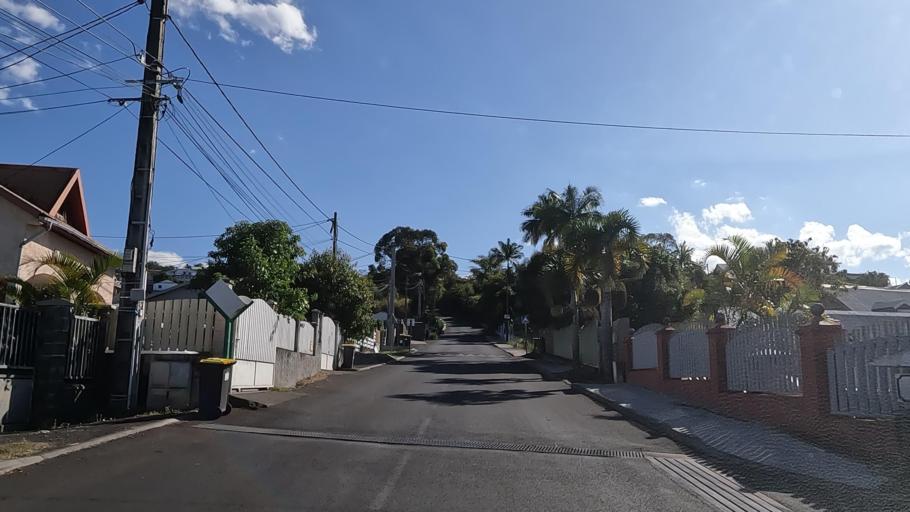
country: RE
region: Reunion
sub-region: Reunion
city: Le Tampon
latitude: -21.2581
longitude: 55.5141
